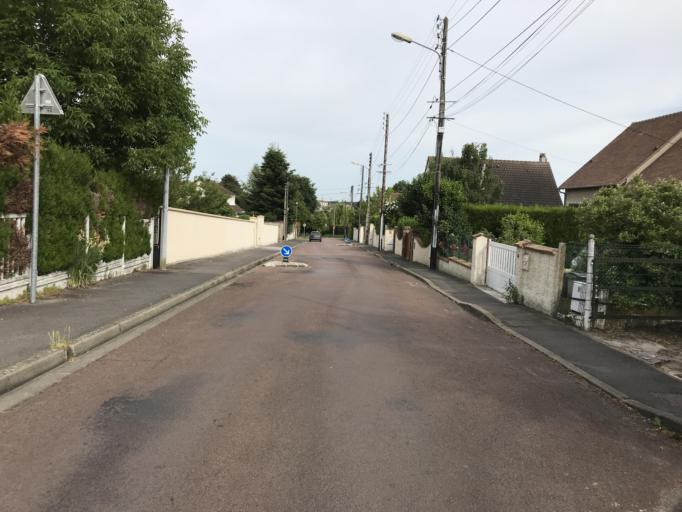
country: FR
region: Ile-de-France
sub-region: Departement de l'Essonne
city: Longpont-sur-Orge
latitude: 48.6333
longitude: 2.2861
